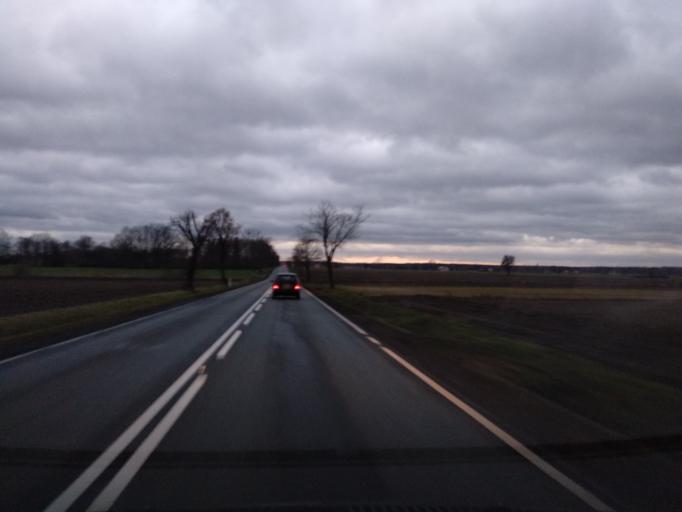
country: PL
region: Greater Poland Voivodeship
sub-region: Powiat koninski
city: Rychwal
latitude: 52.0495
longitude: 18.1627
